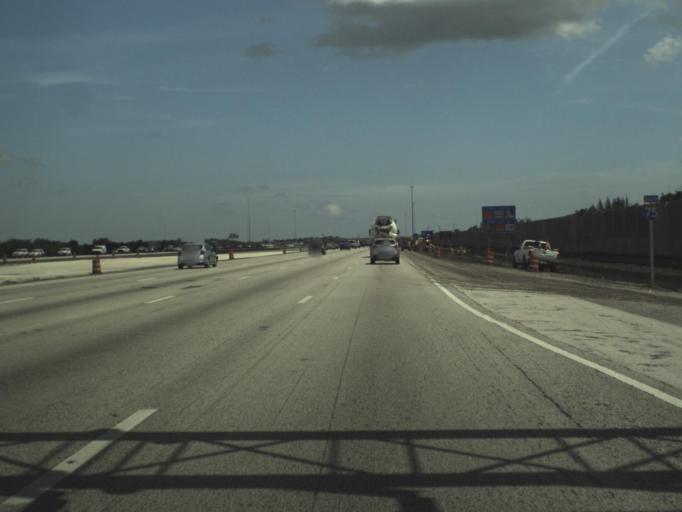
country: US
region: Florida
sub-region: Broward County
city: Sunshine Ranches
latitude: 26.0189
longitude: -80.3468
